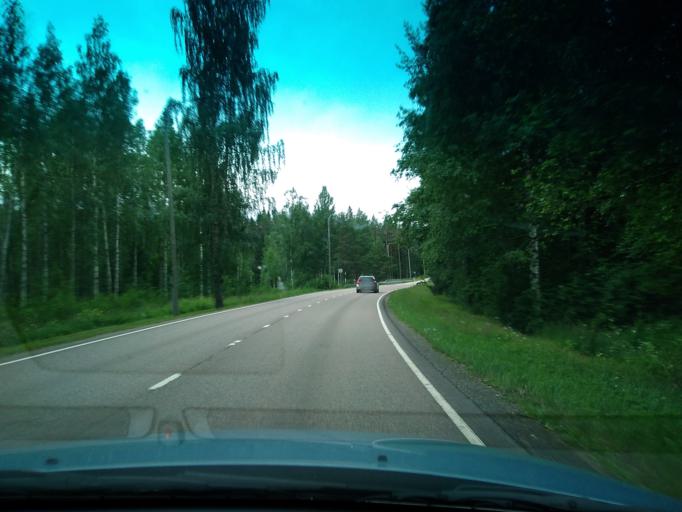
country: FI
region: Central Finland
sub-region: Keuruu
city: Multia
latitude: 62.4004
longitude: 24.7918
